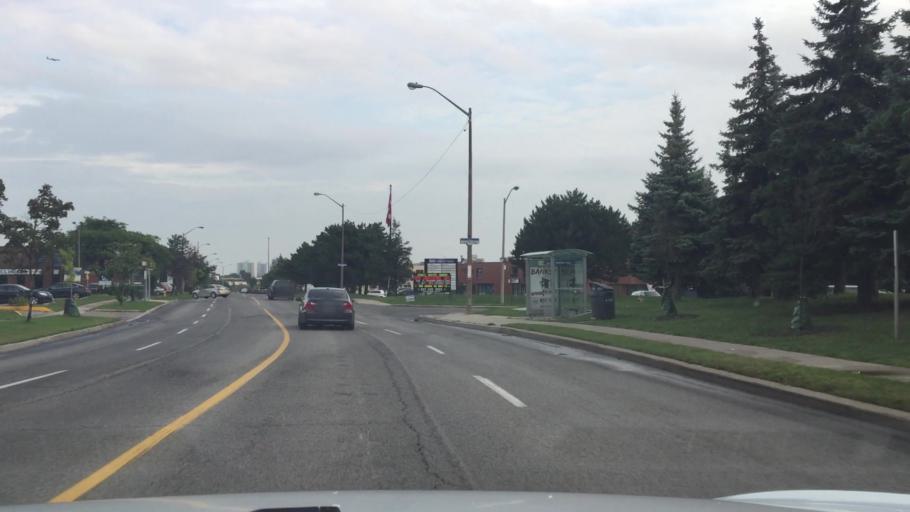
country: CA
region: Ontario
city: Concord
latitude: 43.7499
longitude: -79.5332
